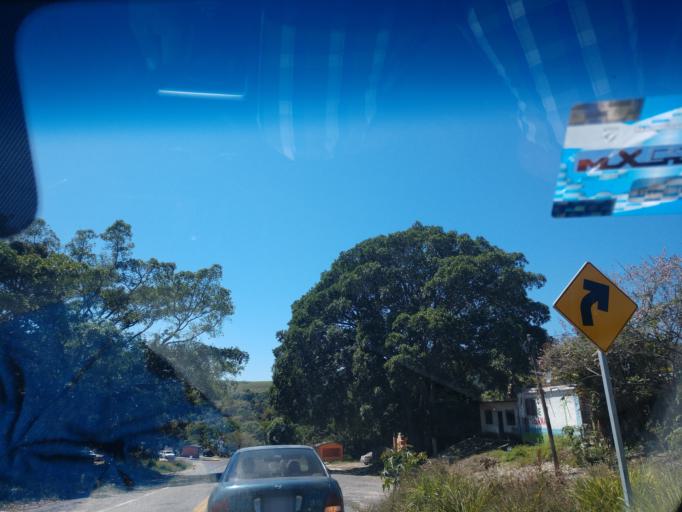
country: MX
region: Nayarit
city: Xalisco
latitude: 21.3676
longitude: -104.9151
